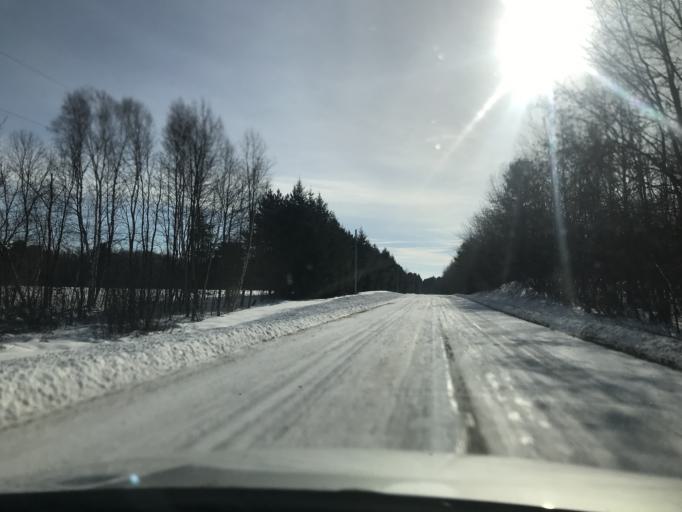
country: US
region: Wisconsin
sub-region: Oconto County
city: Gillett
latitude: 45.1264
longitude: -88.2498
